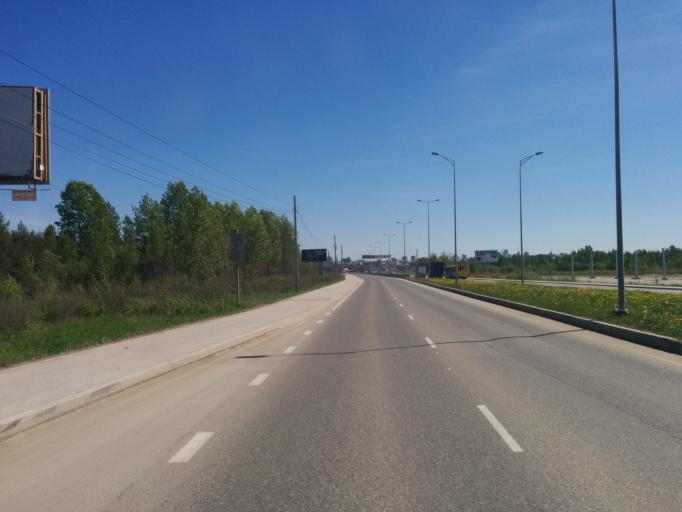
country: RU
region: Perm
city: Perm
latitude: 58.0341
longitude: 56.2037
